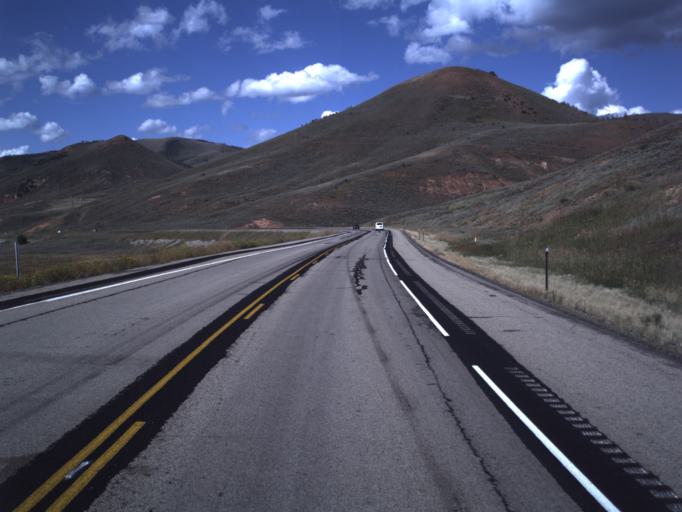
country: US
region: Utah
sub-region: Wasatch County
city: Heber
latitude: 40.2082
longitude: -111.1036
